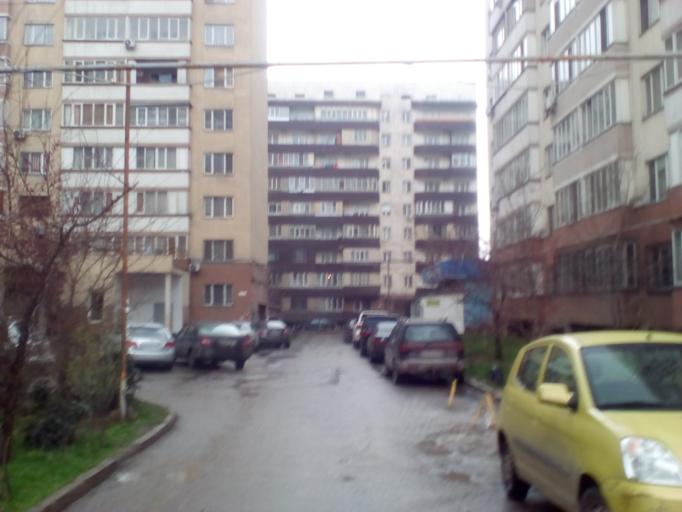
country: KZ
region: Almaty Qalasy
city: Almaty
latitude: 43.2411
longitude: 76.8249
